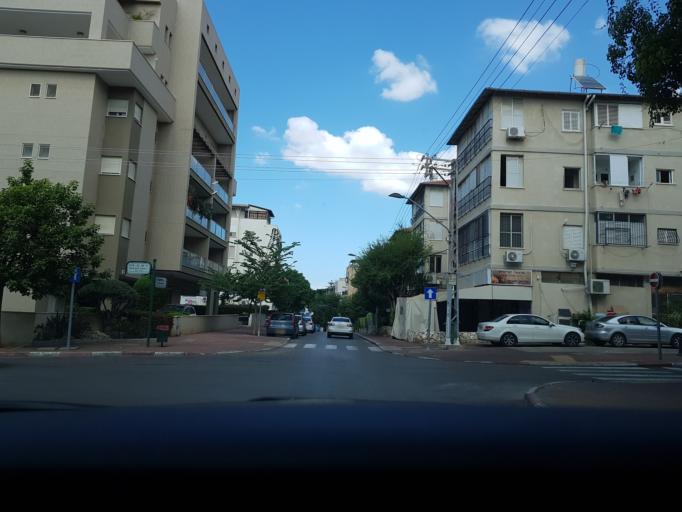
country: IL
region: Central District
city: Ness Ziona
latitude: 31.8991
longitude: 34.8073
